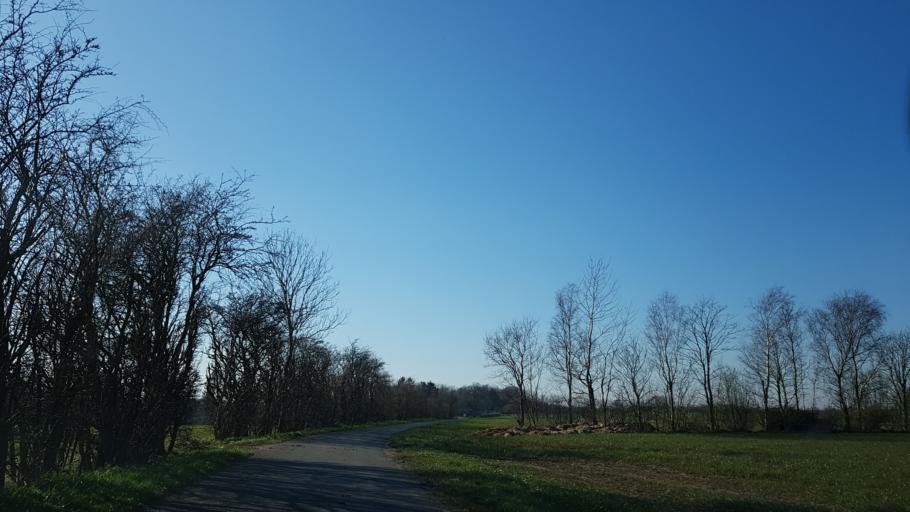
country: DK
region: South Denmark
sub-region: Kolding Kommune
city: Vamdrup
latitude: 55.4162
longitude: 9.2363
